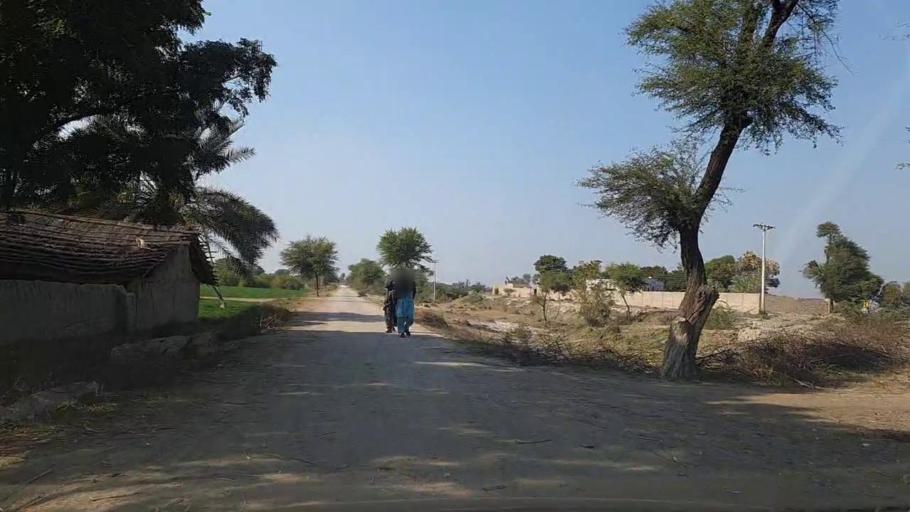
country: PK
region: Sindh
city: Daur
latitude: 26.3810
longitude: 68.3300
